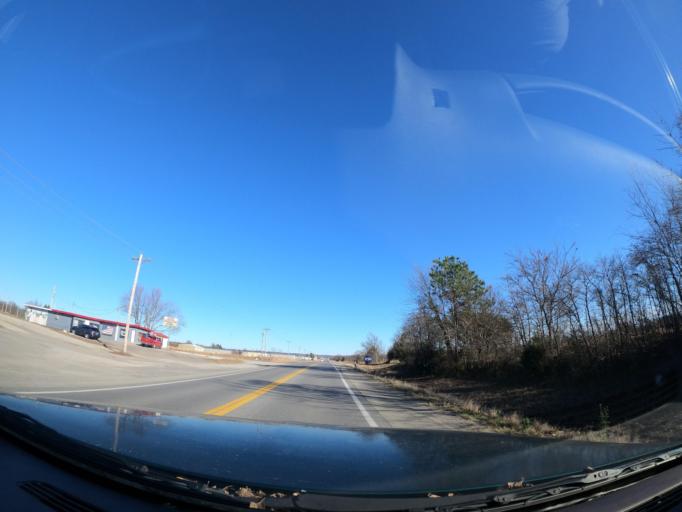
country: US
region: Oklahoma
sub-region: Pittsburg County
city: Longtown
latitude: 35.2392
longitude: -95.5258
